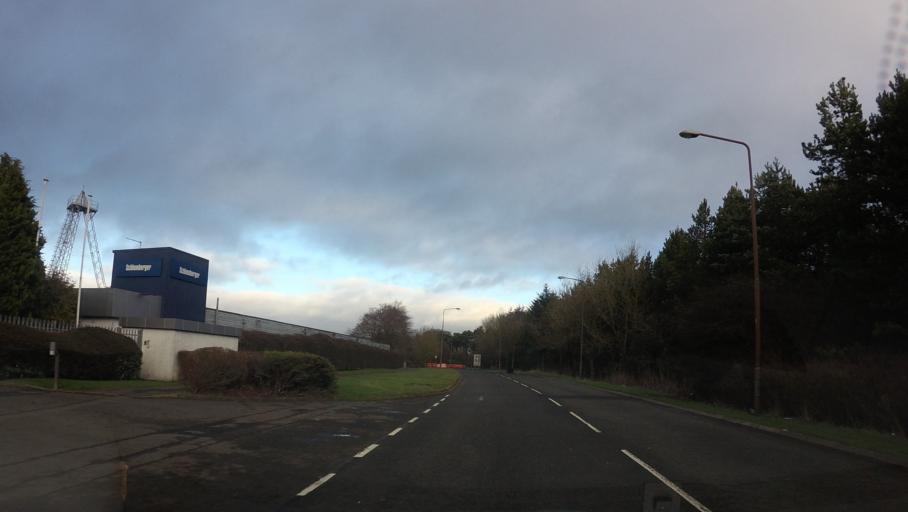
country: GB
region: Scotland
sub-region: West Lothian
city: West Calder
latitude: 55.9035
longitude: -3.5757
